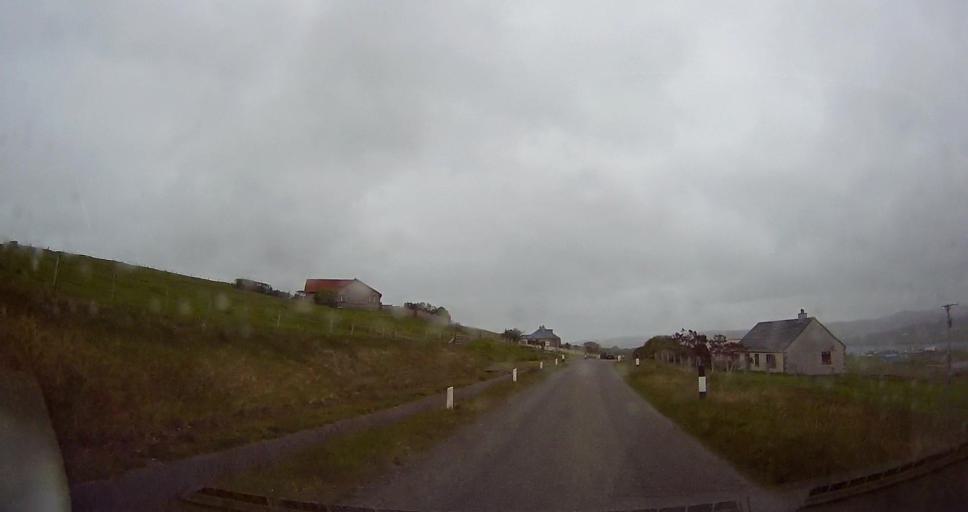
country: GB
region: Scotland
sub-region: Shetland Islands
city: Lerwick
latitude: 60.2783
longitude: -1.3896
